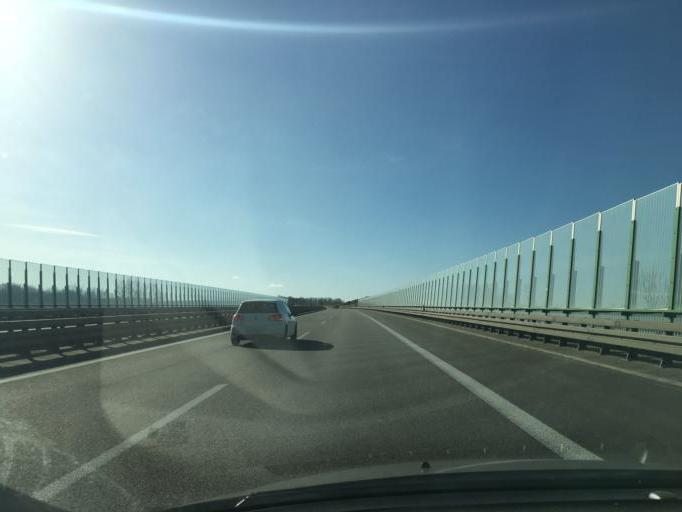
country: DE
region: Saxony
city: Penig
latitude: 50.9193
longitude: 12.6951
